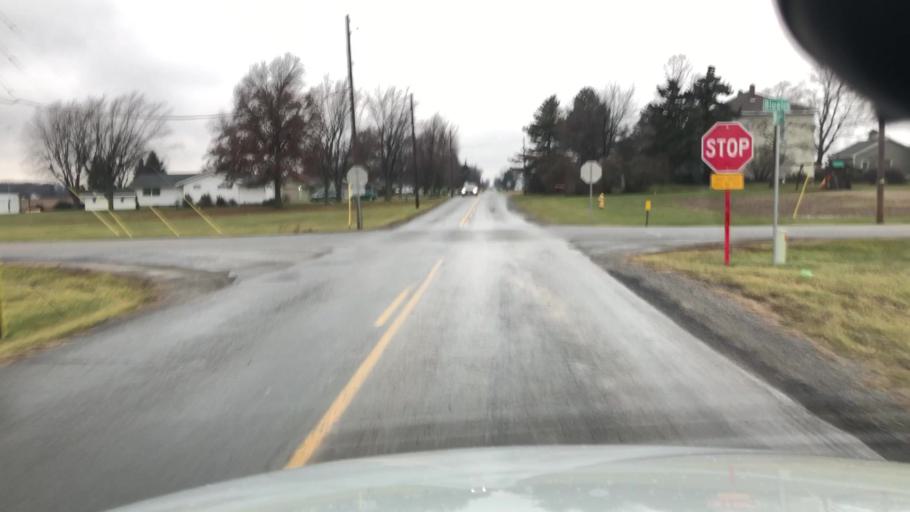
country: US
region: Ohio
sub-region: Allen County
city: Lima
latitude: 40.7890
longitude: -84.0131
